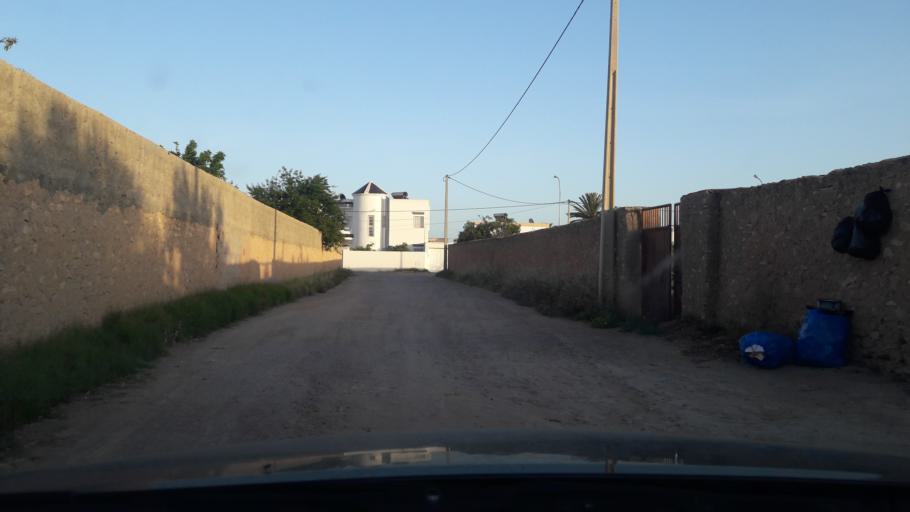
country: TN
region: Safaqis
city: Al Qarmadah
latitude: 34.7915
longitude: 10.7531
